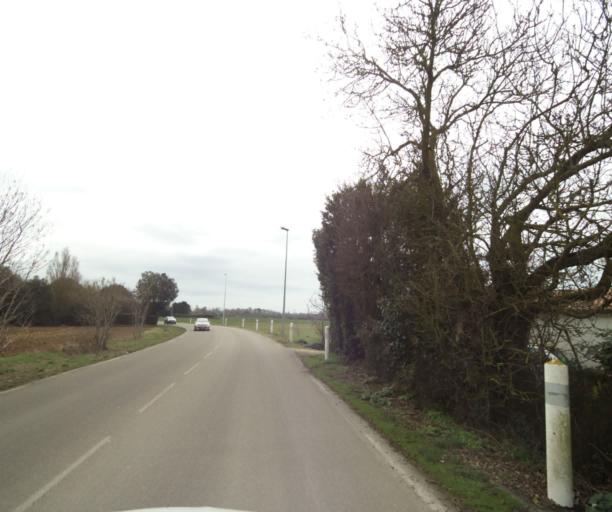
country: FR
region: Poitou-Charentes
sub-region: Departement de la Charente-Maritime
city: Nieul-sur-Mer
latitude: 46.1870
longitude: -1.1805
